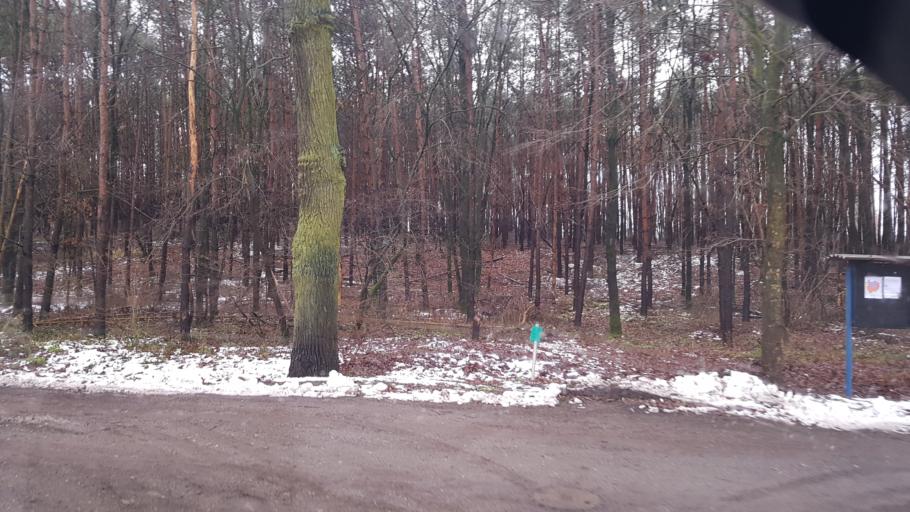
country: DE
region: Brandenburg
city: Schenkendobern
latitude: 51.9680
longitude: 14.5763
